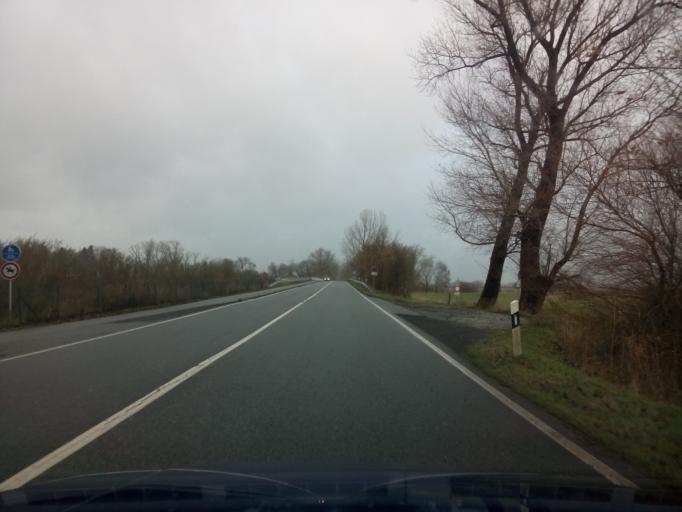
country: DE
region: Lower Saxony
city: Osterholz-Scharmbeck
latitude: 53.2008
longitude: 8.8206
